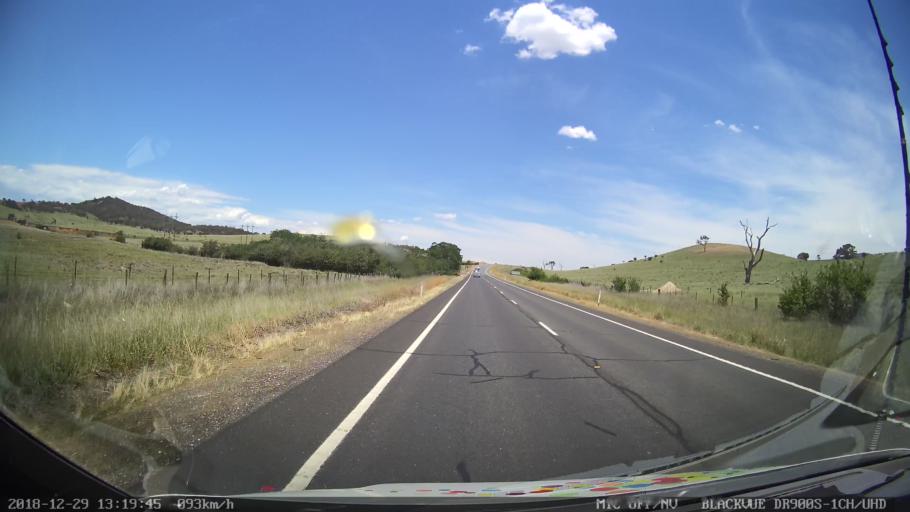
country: AU
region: Australian Capital Territory
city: Macarthur
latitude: -35.7698
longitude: 149.1616
